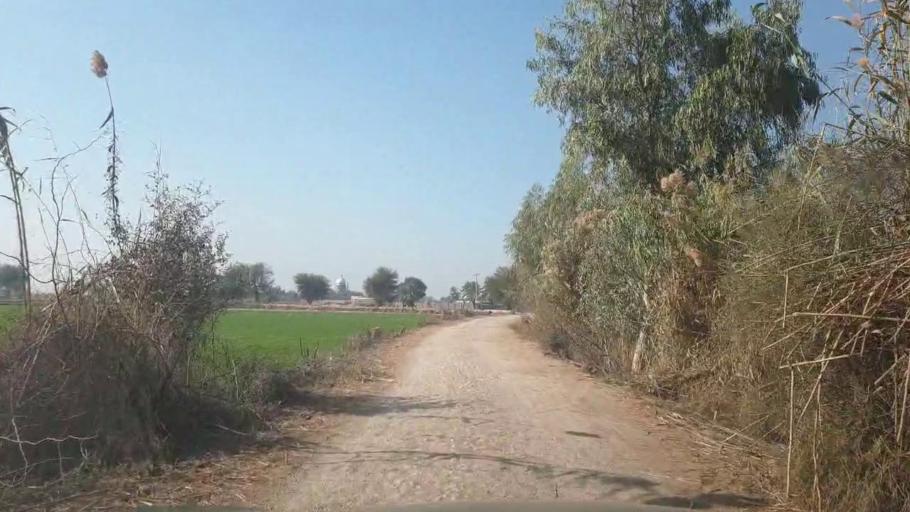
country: PK
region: Sindh
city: Mirpur Mathelo
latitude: 27.9893
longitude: 69.4695
